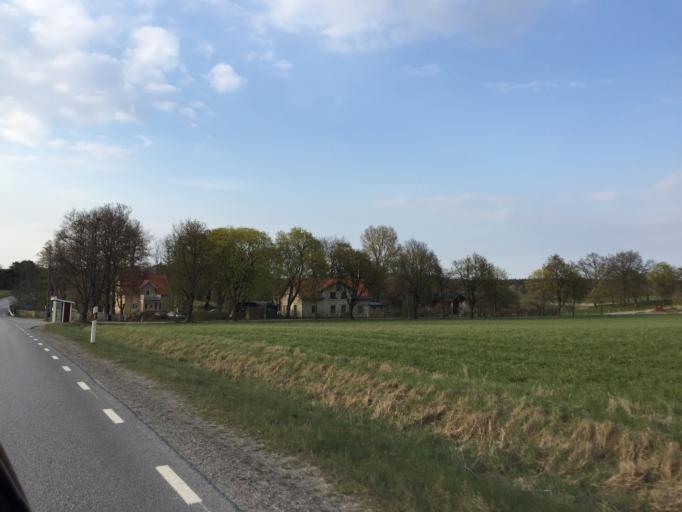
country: SE
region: Stockholm
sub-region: Sodertalje Kommun
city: Pershagen
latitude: 59.0806
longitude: 17.6083
